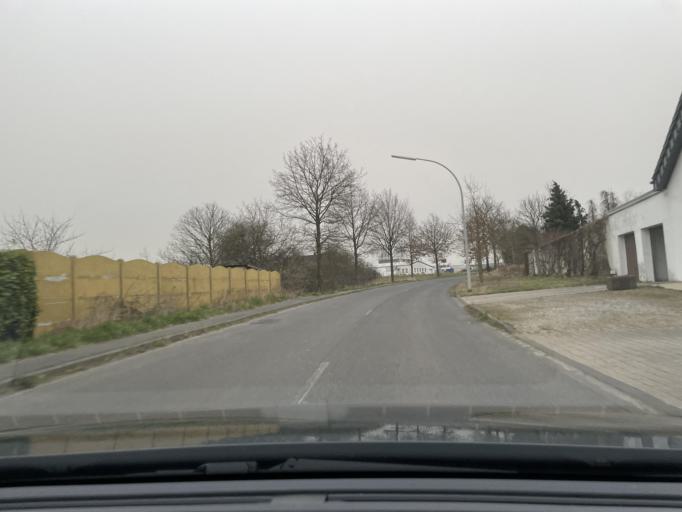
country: DE
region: North Rhine-Westphalia
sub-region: Regierungsbezirk Dusseldorf
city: Monchengladbach
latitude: 51.1114
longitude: 6.4205
